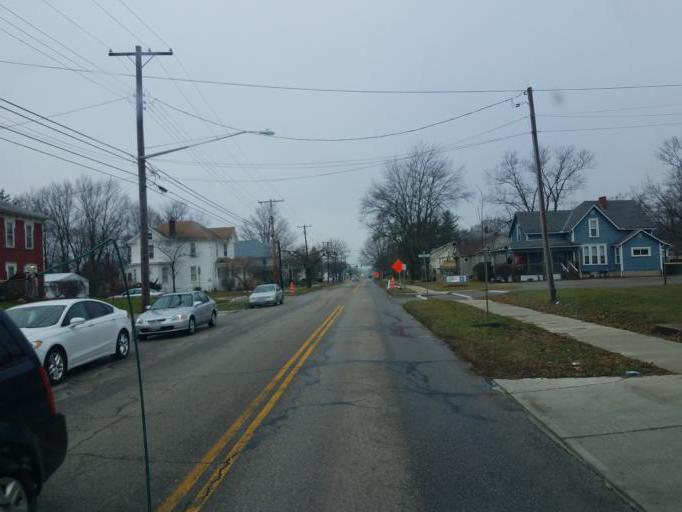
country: US
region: Ohio
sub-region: Union County
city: Marysville
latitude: 40.2375
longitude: -83.3778
